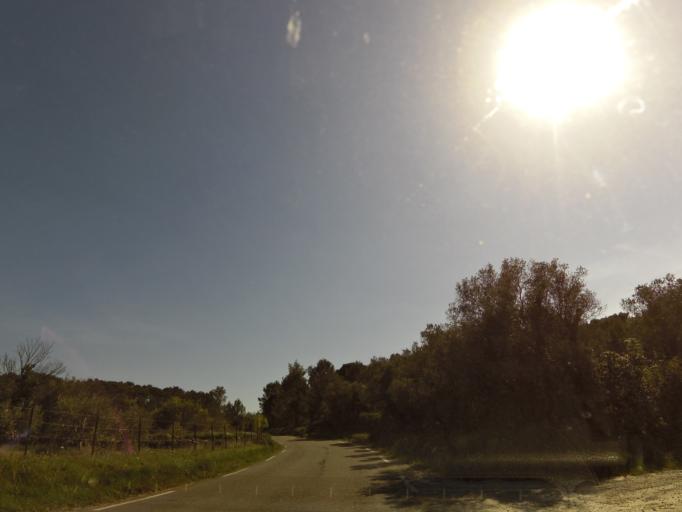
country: FR
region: Languedoc-Roussillon
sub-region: Departement du Gard
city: Congenies
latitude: 43.7669
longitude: 4.1595
